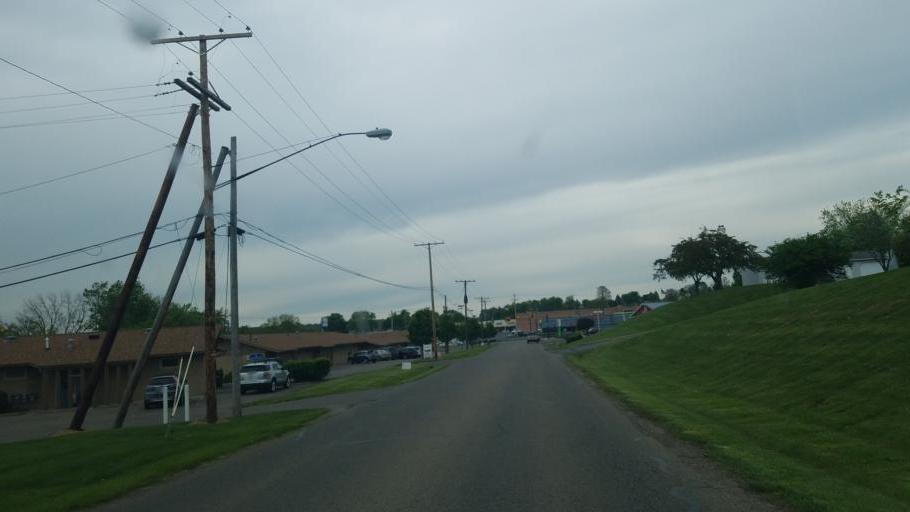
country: US
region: Ohio
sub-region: Knox County
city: Mount Vernon
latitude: 40.3975
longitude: -82.4597
